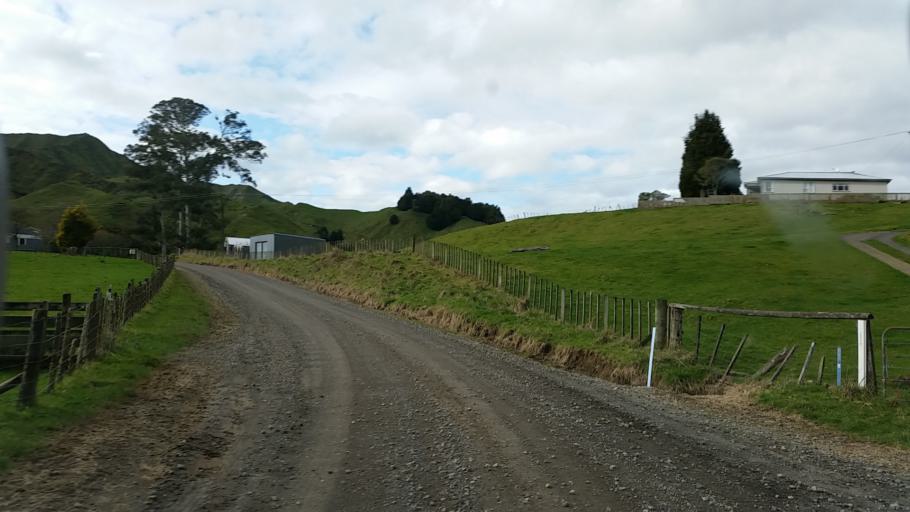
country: NZ
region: Taranaki
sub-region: New Plymouth District
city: Waitara
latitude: -39.1620
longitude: 174.5767
